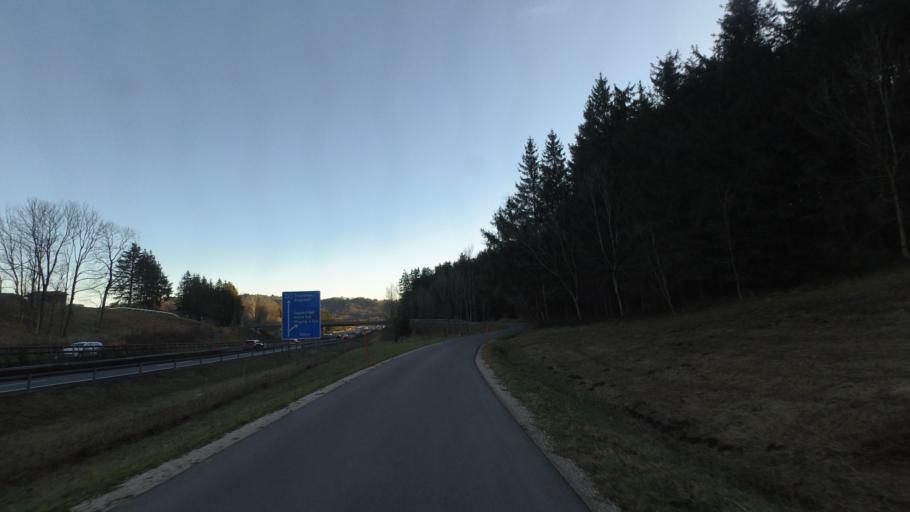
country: DE
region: Bavaria
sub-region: Upper Bavaria
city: Siegsdorf
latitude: 47.8274
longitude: 12.6224
